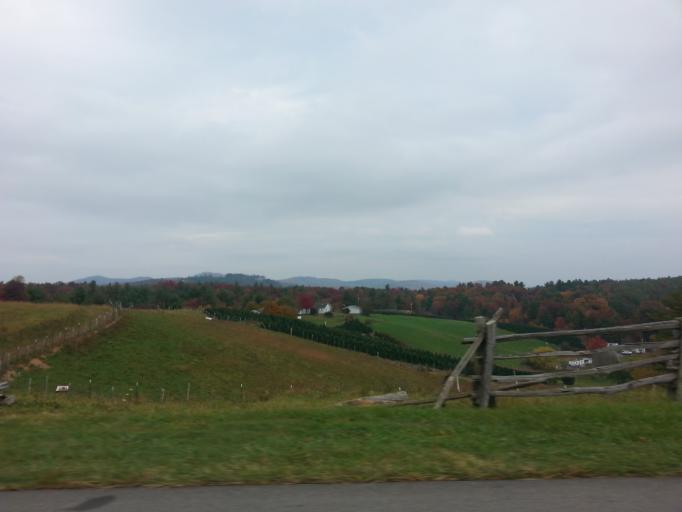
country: US
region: North Carolina
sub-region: Ashe County
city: Jefferson
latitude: 36.3426
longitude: -81.3745
